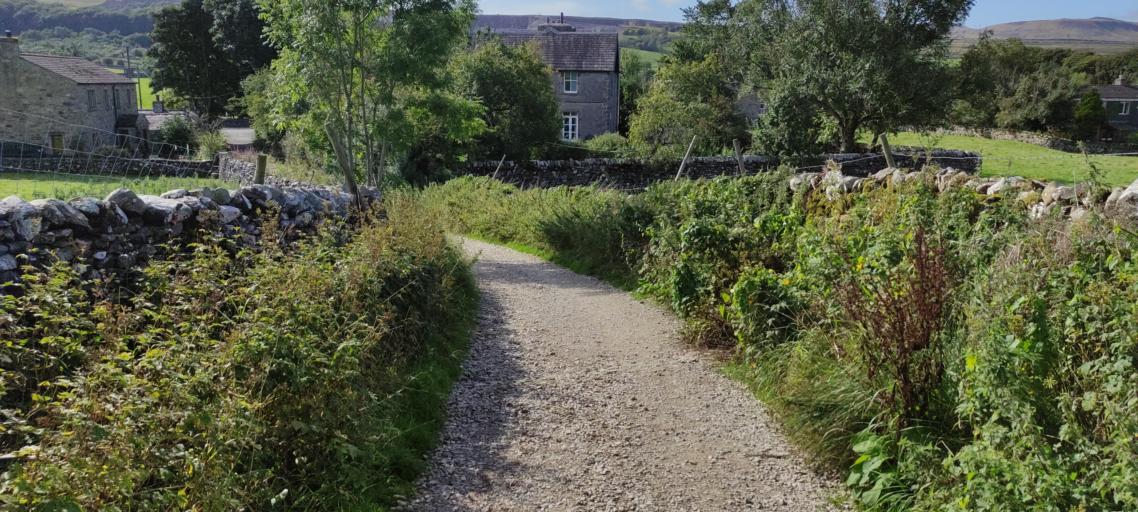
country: GB
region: England
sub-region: North Yorkshire
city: Settle
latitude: 54.1478
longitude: -2.2928
